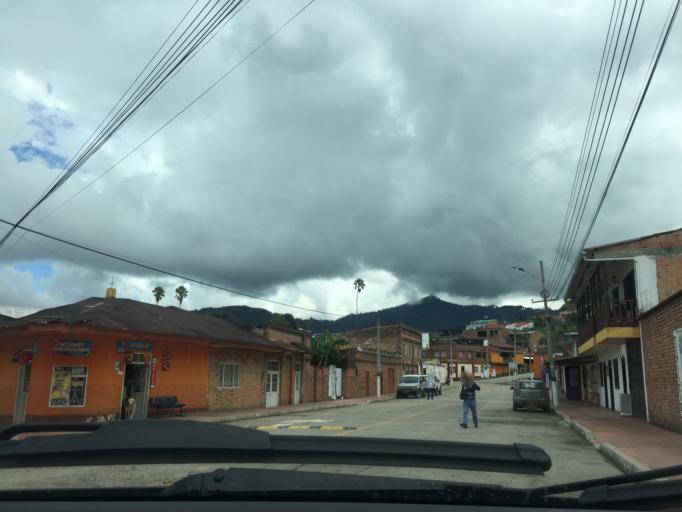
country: CO
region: Cundinamarca
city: Supata
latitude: 5.0602
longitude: -74.2366
